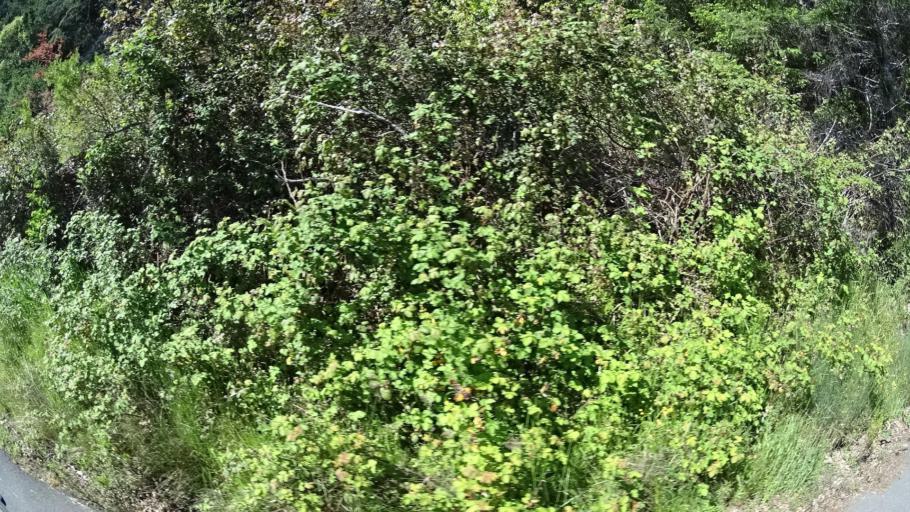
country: US
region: California
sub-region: Humboldt County
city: Rio Dell
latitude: 40.2372
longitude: -124.1598
